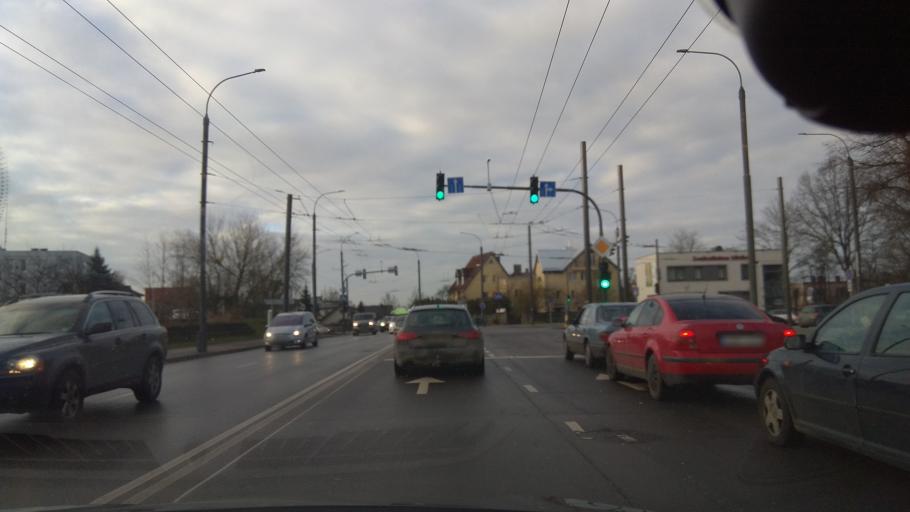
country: LT
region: Kauno apskritis
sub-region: Kaunas
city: Eiguliai
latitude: 54.9162
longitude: 23.9246
